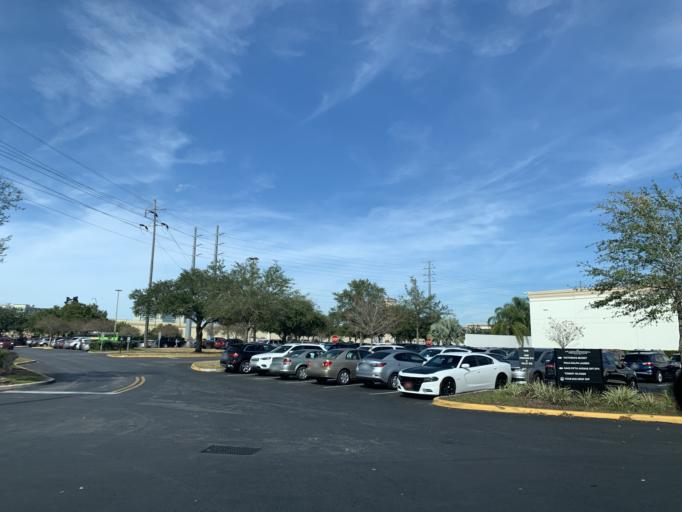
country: US
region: Florida
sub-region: Orange County
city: Tangelo Park
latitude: 28.4723
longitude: -81.4540
